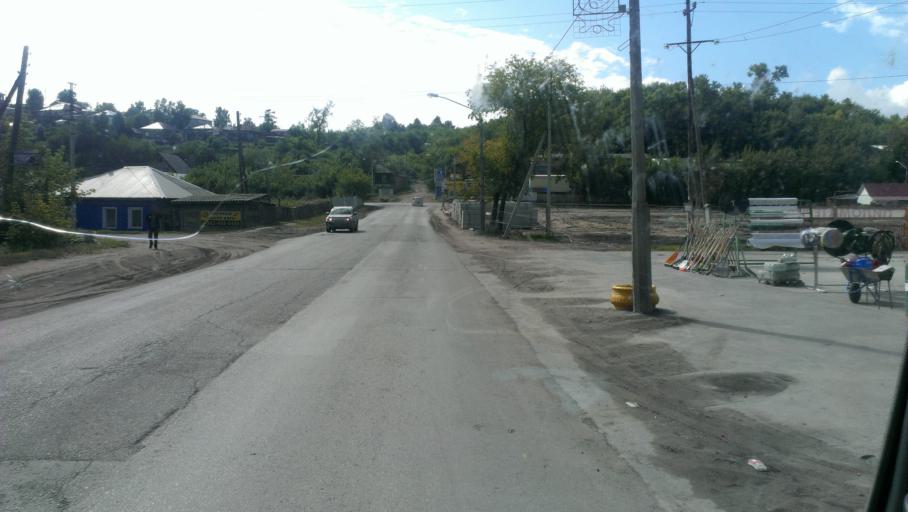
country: RU
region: Altai Krai
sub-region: Gorod Barnaulskiy
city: Barnaul
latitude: 53.3203
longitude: 83.7699
